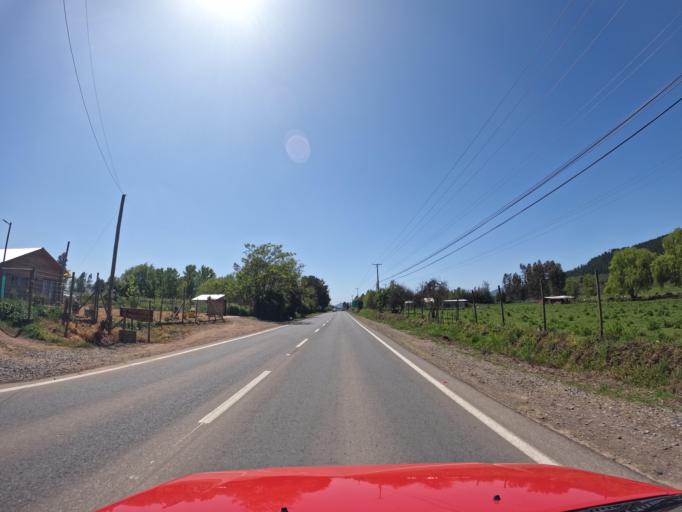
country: CL
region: Maule
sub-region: Provincia de Linares
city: Colbun
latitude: -35.7269
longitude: -71.4187
